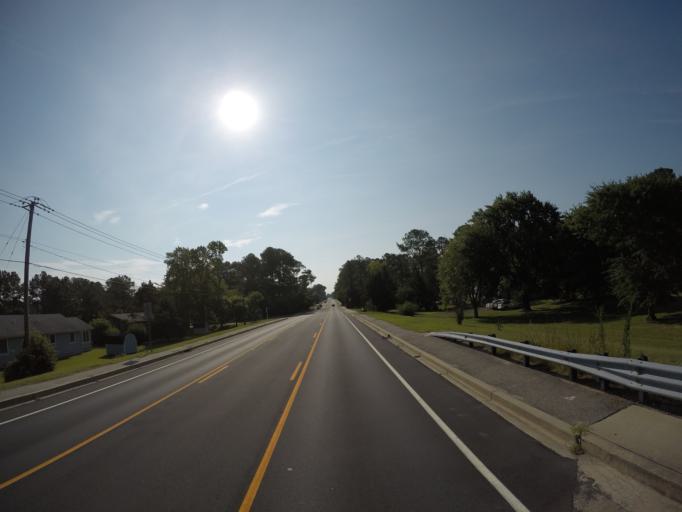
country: US
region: Delaware
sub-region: Sussex County
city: Ocean View
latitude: 38.5425
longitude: -75.0804
